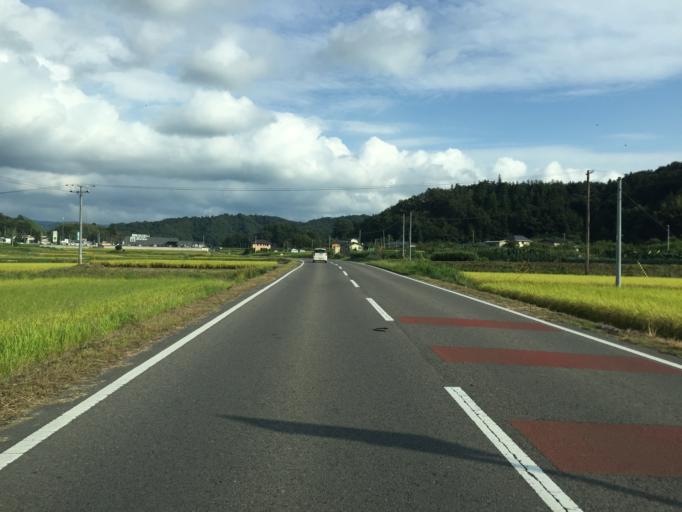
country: JP
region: Fukushima
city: Fukushima-shi
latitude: 37.6712
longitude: 140.5676
